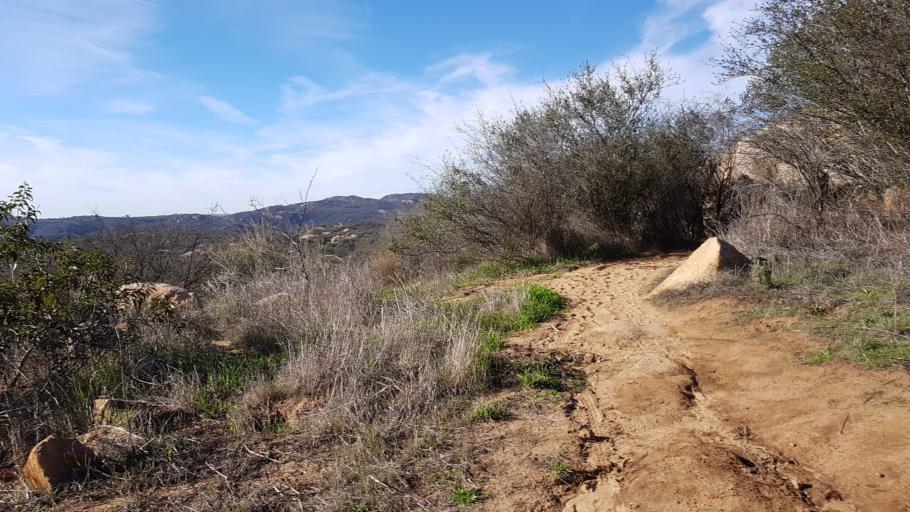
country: US
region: California
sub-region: San Diego County
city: Valley Center
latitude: 33.1794
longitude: -117.0337
